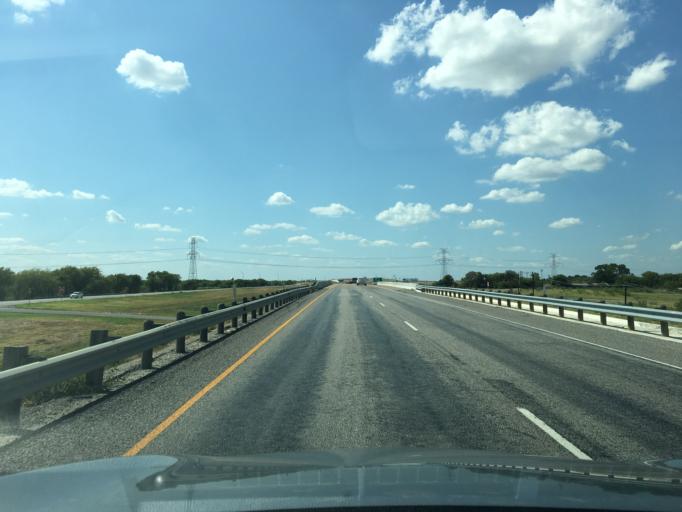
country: US
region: Texas
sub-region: Tarrant County
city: Mansfield
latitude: 32.5162
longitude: -97.0720
